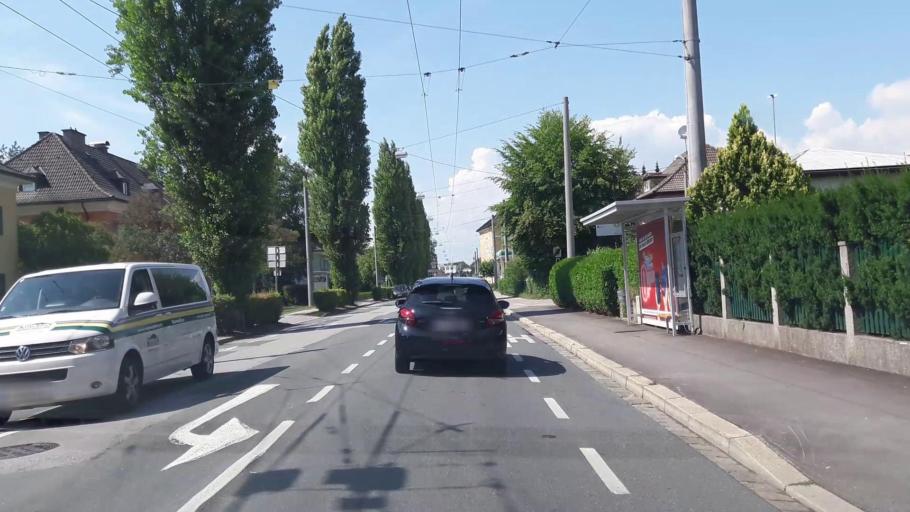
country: AT
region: Salzburg
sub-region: Salzburg Stadt
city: Salzburg
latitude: 47.8030
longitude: 13.0289
